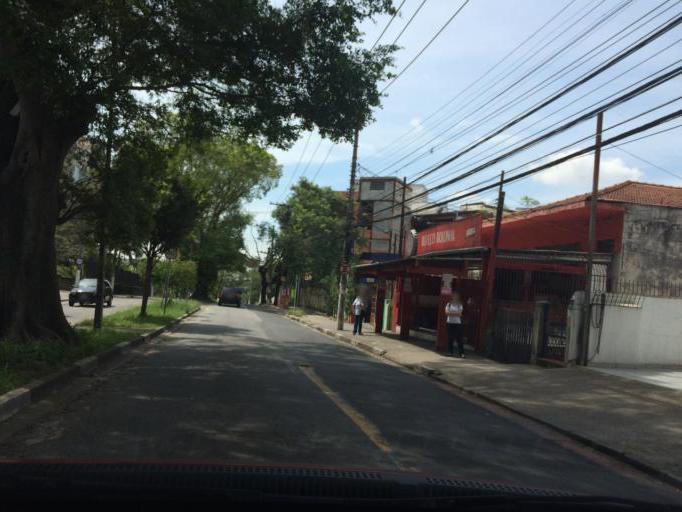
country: BR
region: Sao Paulo
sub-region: Osasco
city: Osasco
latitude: -23.5482
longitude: -46.7481
